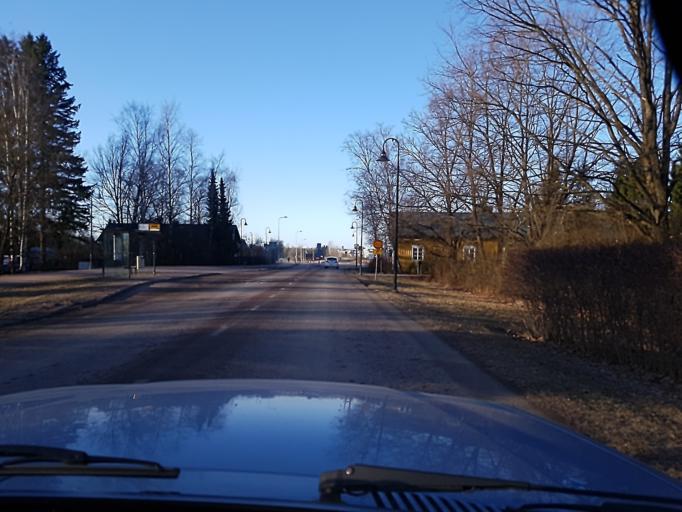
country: FI
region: Uusimaa
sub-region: Helsinki
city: Vantaa
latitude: 60.2822
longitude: 24.9832
